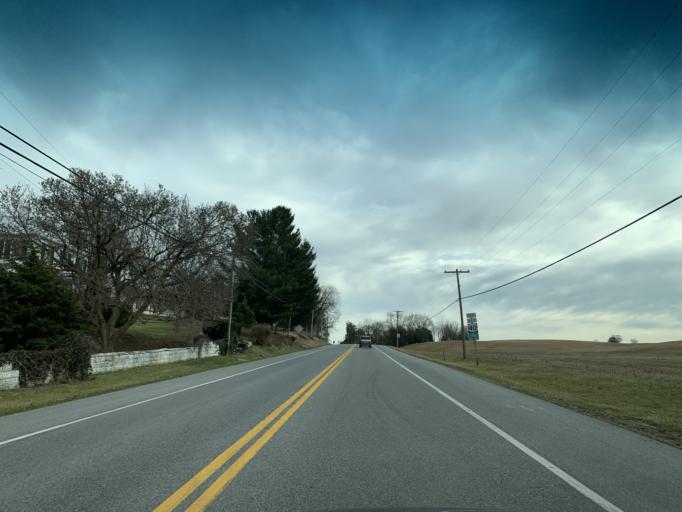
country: US
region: Maryland
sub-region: Washington County
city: Boonsboro
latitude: 39.5457
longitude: -77.6766
